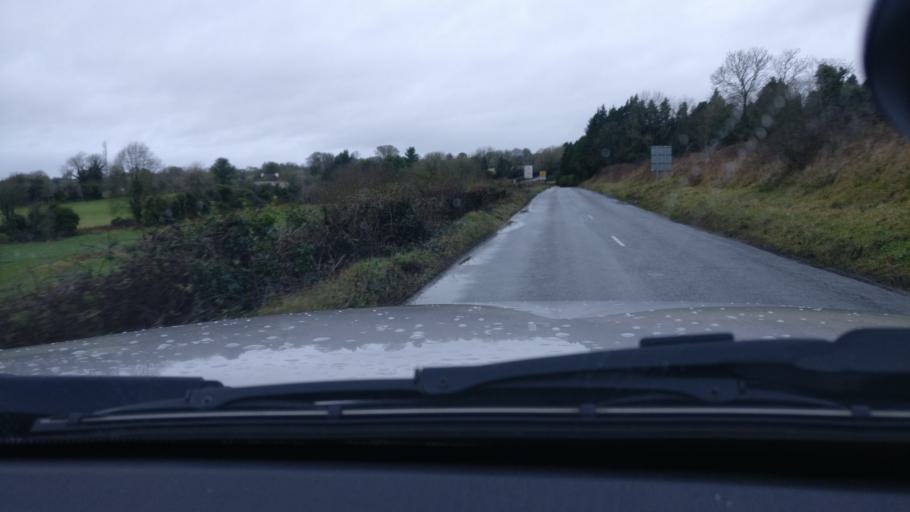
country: IE
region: Leinster
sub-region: An Longfort
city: Granard
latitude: 53.7932
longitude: -7.3994
